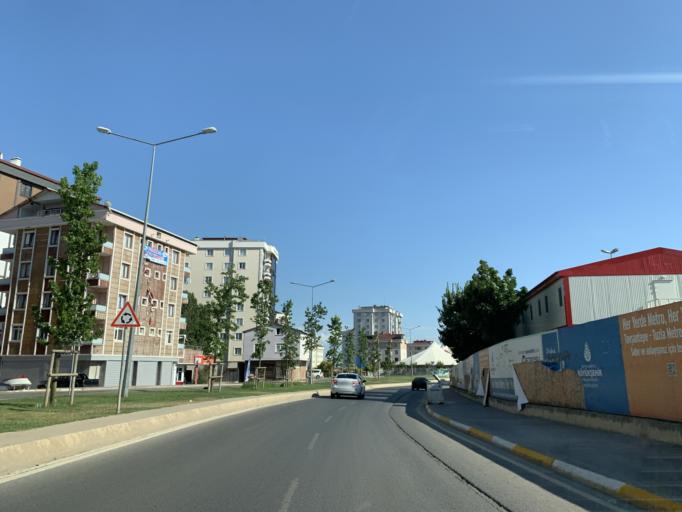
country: TR
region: Istanbul
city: Pendik
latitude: 40.8860
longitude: 29.2654
